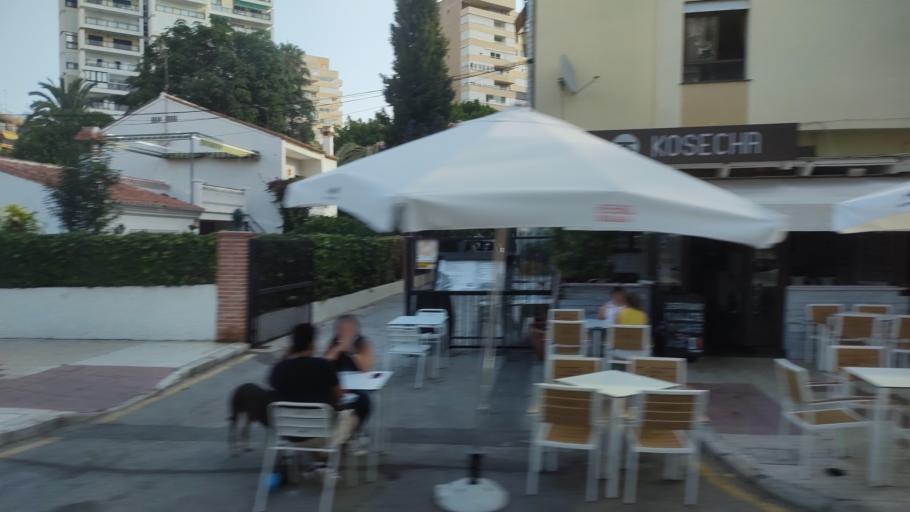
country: ES
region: Andalusia
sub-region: Provincia de Malaga
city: Torremolinos
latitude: 36.6275
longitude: -4.4939
